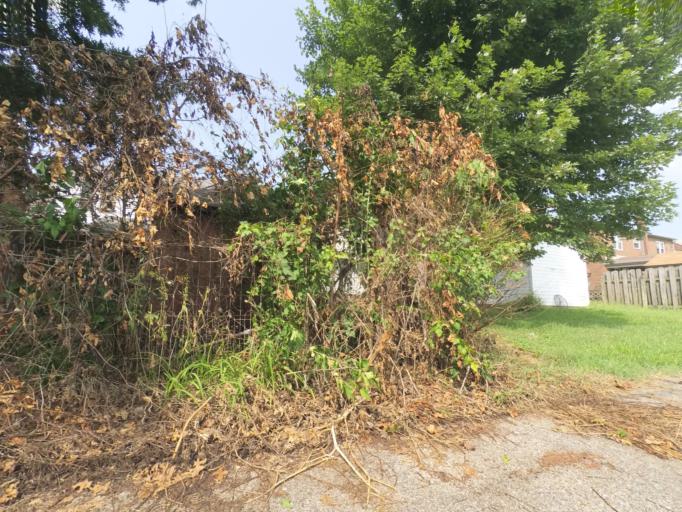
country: US
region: West Virginia
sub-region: Cabell County
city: Huntington
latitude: 38.4053
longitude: -82.4028
